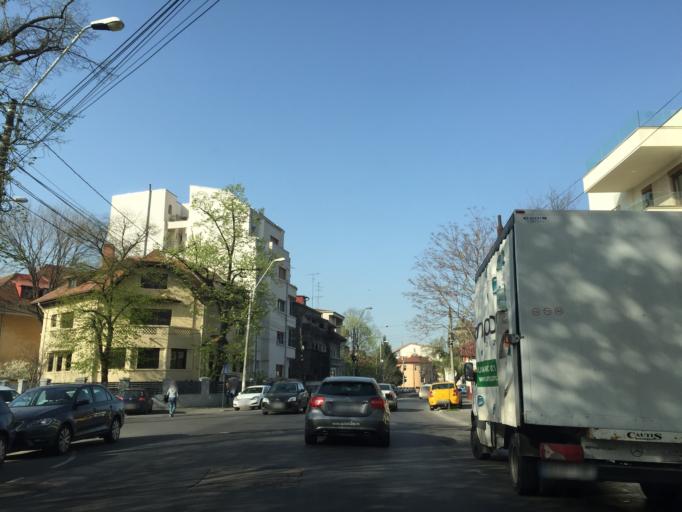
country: RO
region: Bucuresti
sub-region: Municipiul Bucuresti
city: Bucuresti
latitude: 44.4336
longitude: 26.0762
